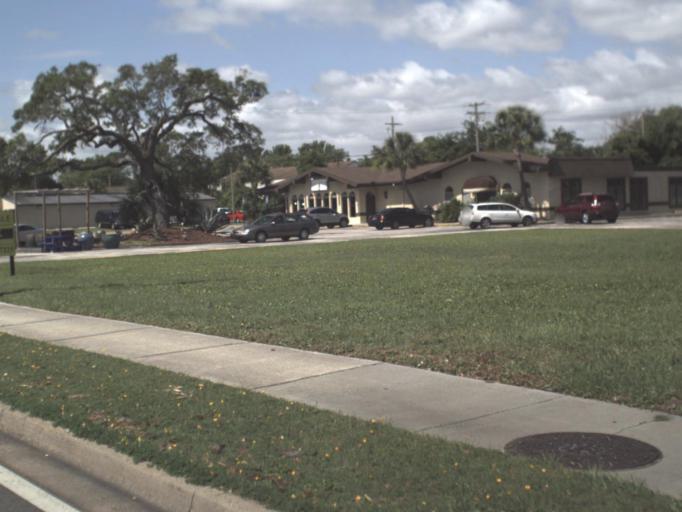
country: US
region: Florida
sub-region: Nassau County
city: Fernandina Beach
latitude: 30.6577
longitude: -81.4608
